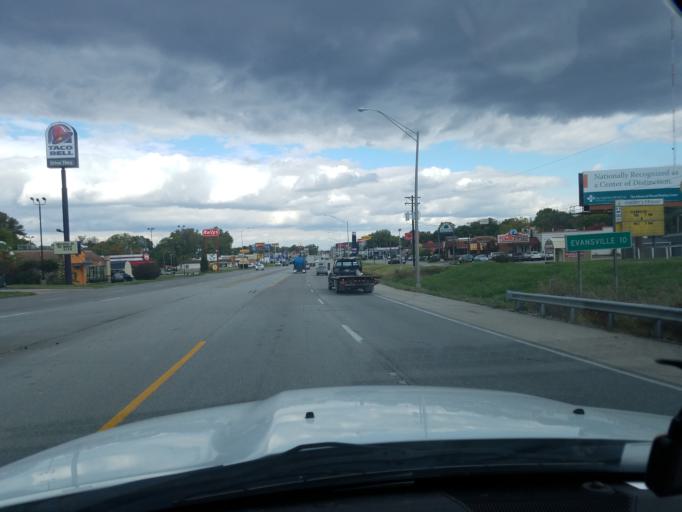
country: US
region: Kentucky
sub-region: Henderson County
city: Henderson
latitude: 37.8615
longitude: -87.5752
